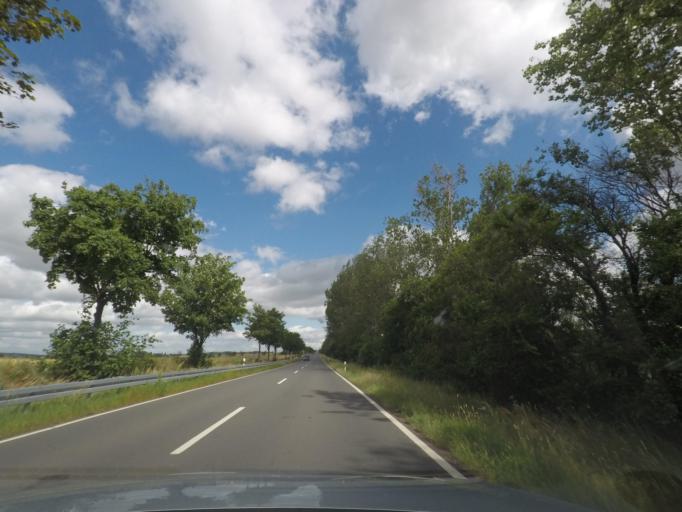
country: DE
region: Saxony-Anhalt
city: Quedlinburg
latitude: 51.8206
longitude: 11.1225
